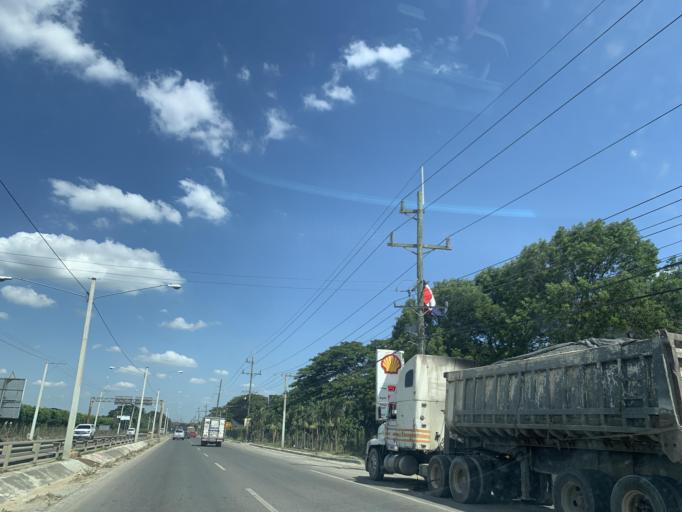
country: DO
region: Santiago
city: Villa Bisono
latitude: 19.5529
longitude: -70.8586
